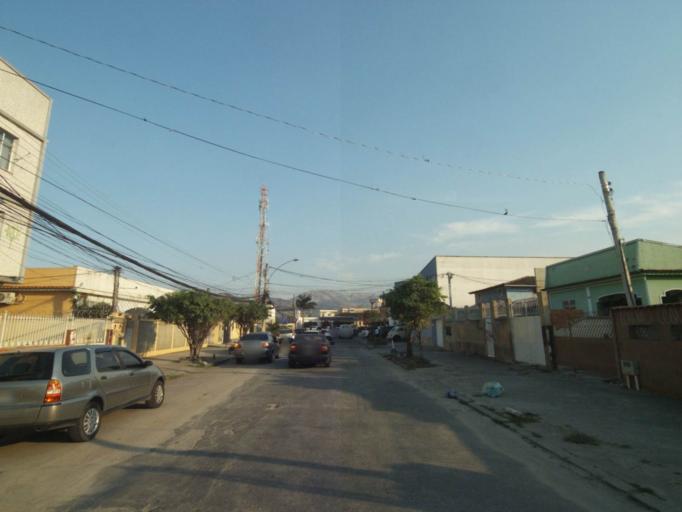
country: BR
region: Rio de Janeiro
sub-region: Nilopolis
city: Nilopolis
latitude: -22.8780
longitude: -43.4275
